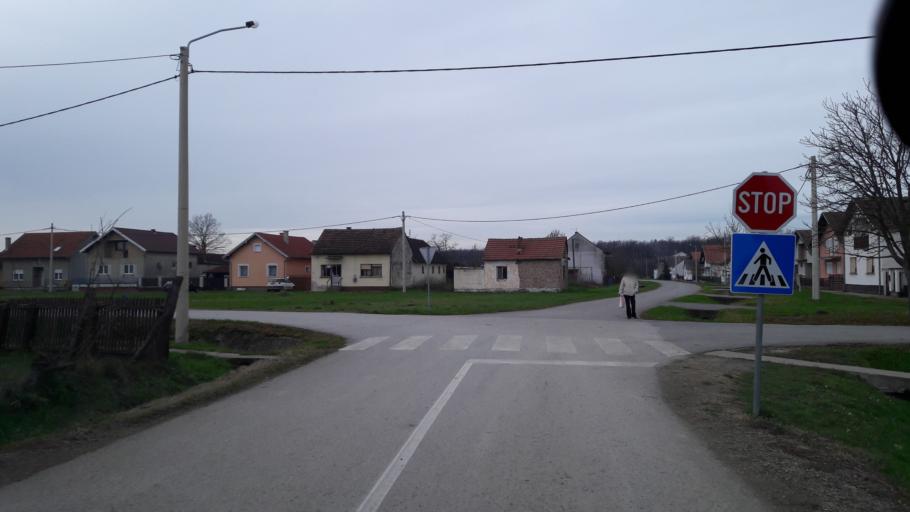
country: HR
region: Osjecko-Baranjska
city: Vladislavci
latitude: 45.4554
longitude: 18.5577
